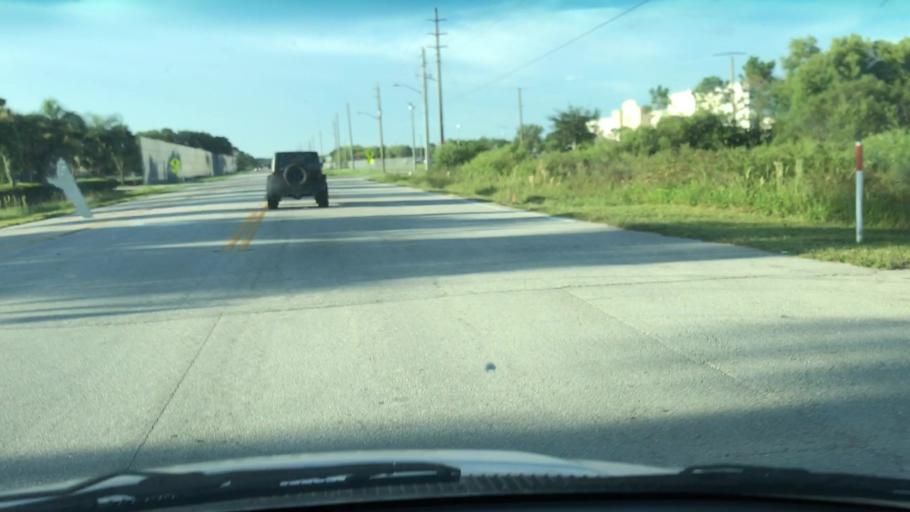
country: US
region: Florida
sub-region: Lee County
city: Villas
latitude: 26.5399
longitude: -81.8470
